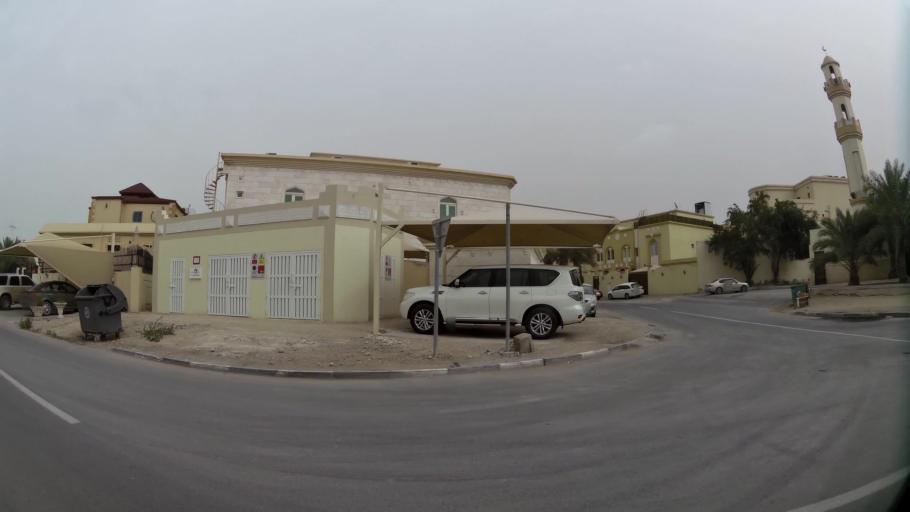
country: QA
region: Baladiyat ad Dawhah
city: Doha
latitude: 25.2402
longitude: 51.5206
